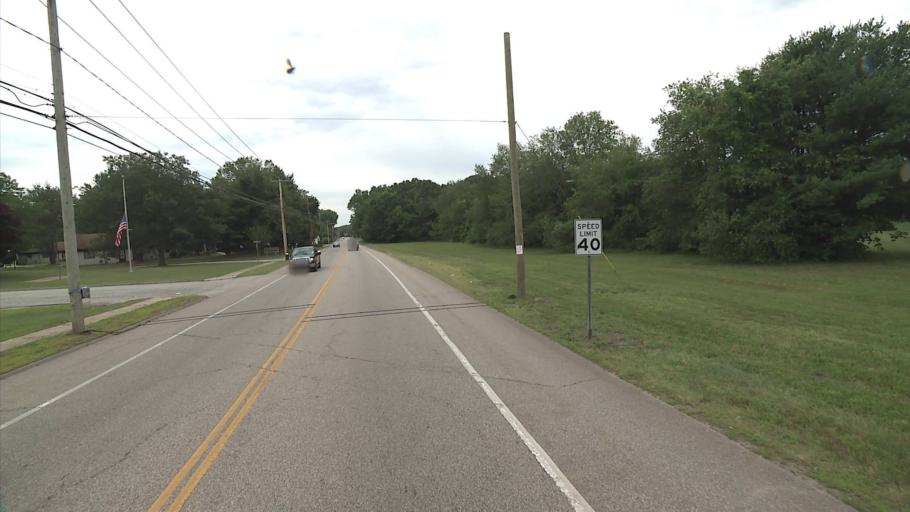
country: US
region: Connecticut
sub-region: New London County
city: Poquonock Bridge
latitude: 41.3523
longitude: -72.0297
